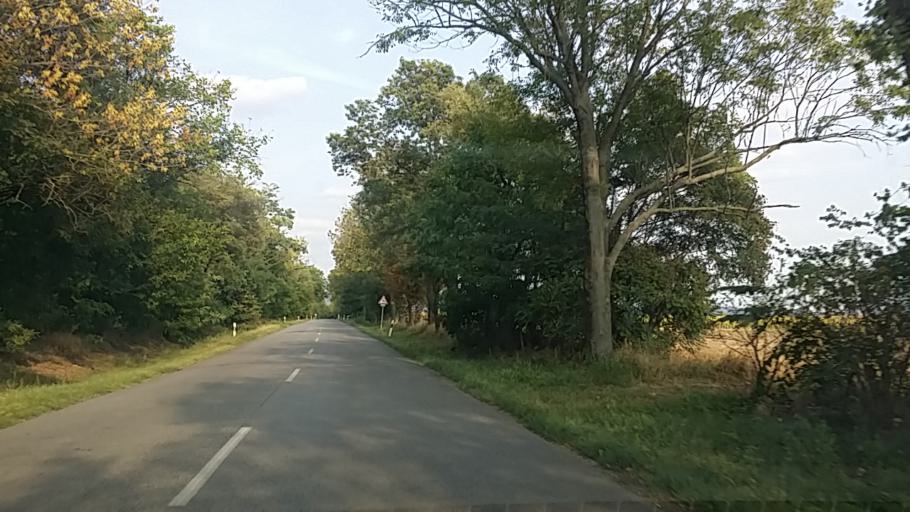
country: HU
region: Komarom-Esztergom
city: Tata
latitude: 47.6279
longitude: 18.2718
